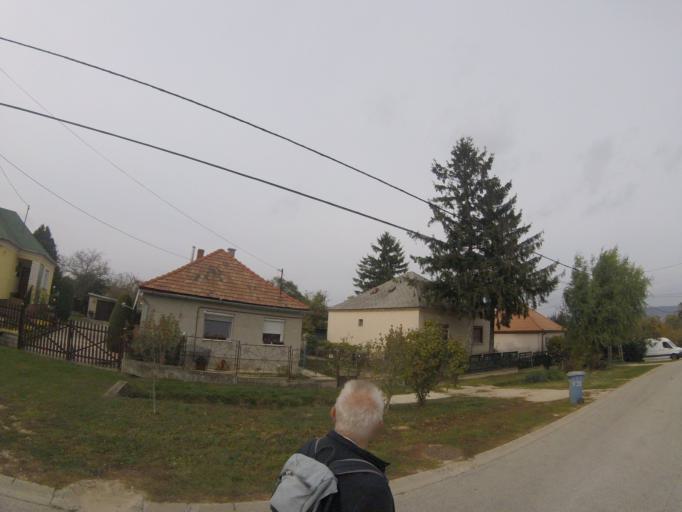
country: HU
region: Fejer
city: Bodajk
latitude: 47.3210
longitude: 18.2239
